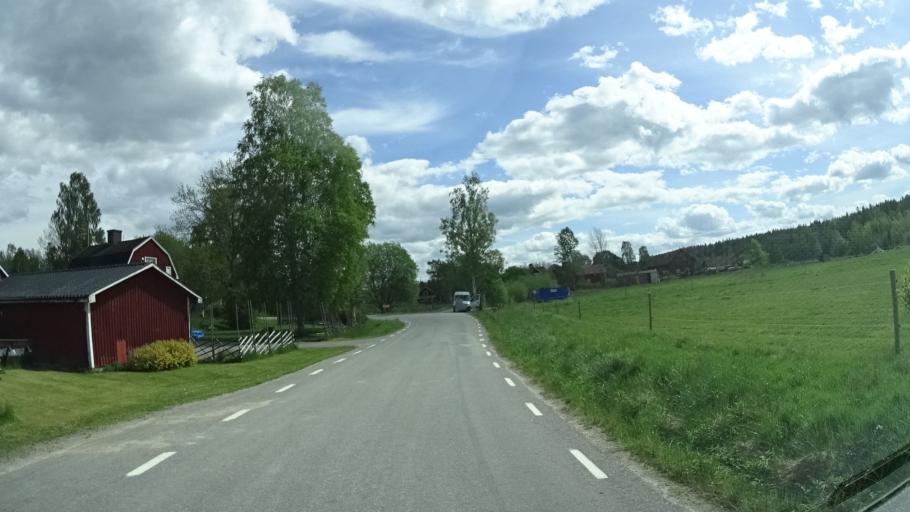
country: SE
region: OEstergoetland
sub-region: Finspangs Kommun
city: Finspang
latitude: 58.6091
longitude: 15.7052
